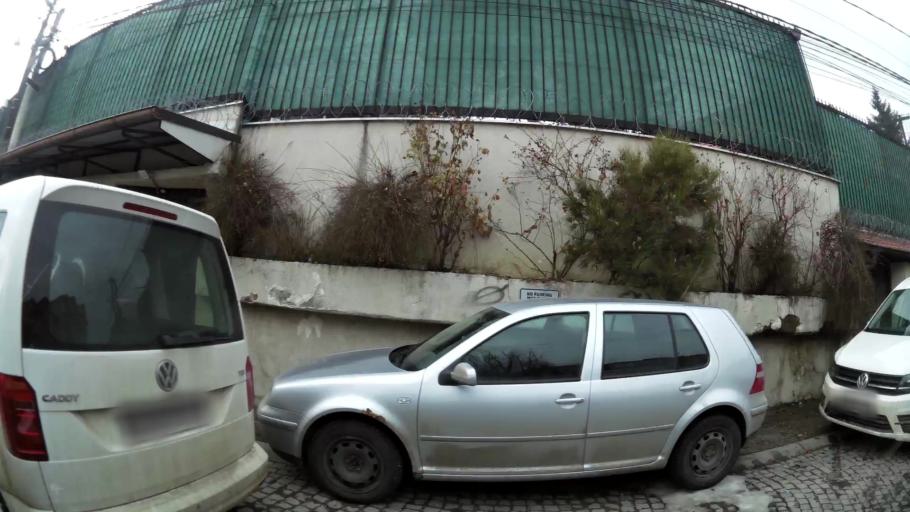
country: XK
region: Pristina
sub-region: Komuna e Prishtines
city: Pristina
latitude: 42.6632
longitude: 21.1512
